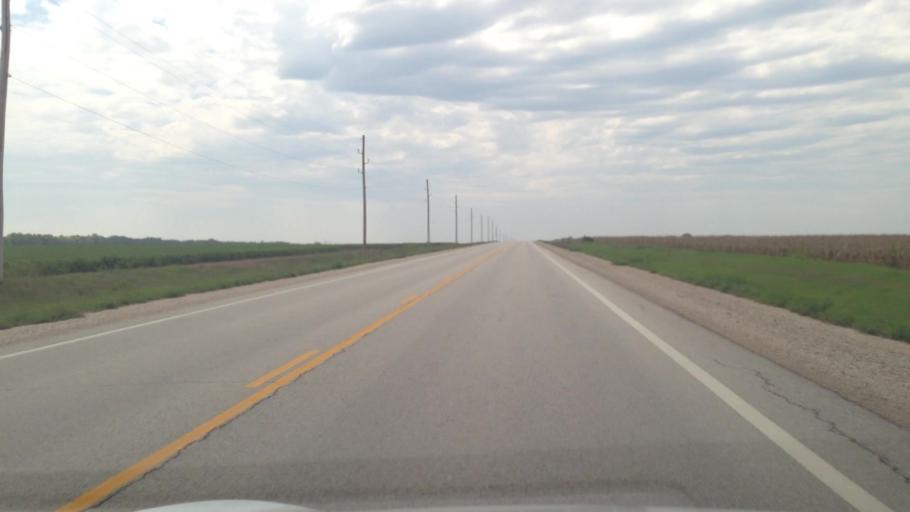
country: US
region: Kansas
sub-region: Anderson County
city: Garnett
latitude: 38.0581
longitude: -95.1695
